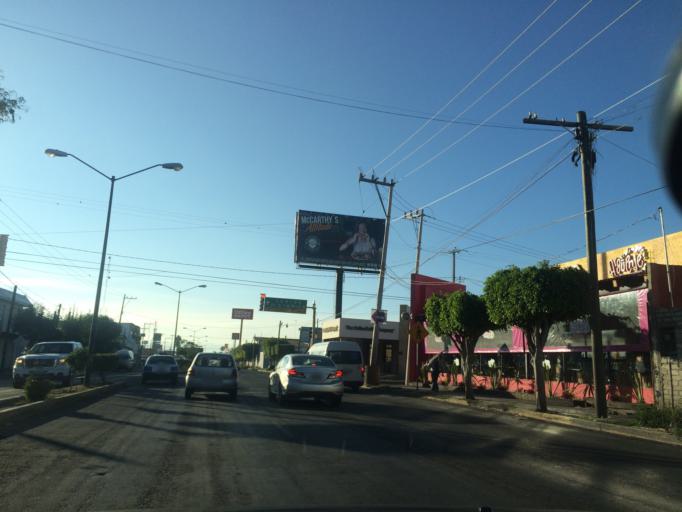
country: MX
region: Puebla
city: Tehuacan
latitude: 18.4652
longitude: -97.4115
